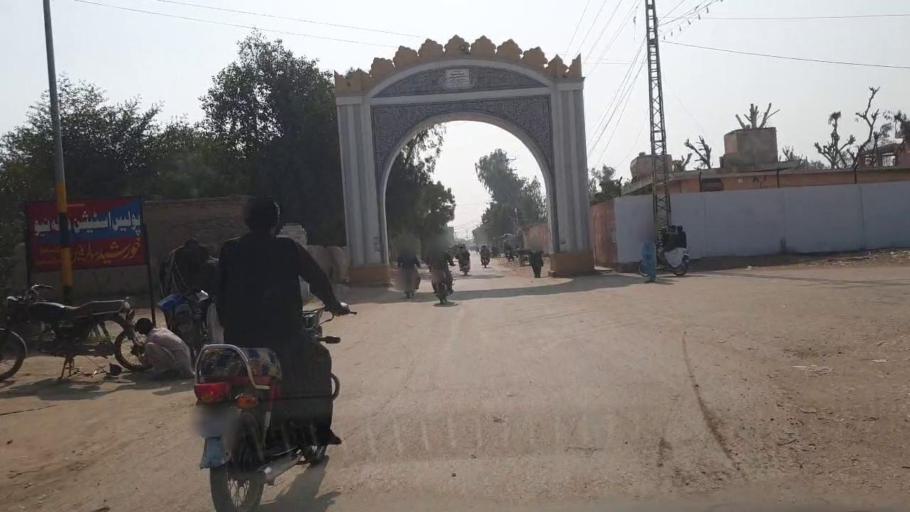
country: PK
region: Sindh
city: Hala
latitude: 25.8198
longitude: 68.4187
